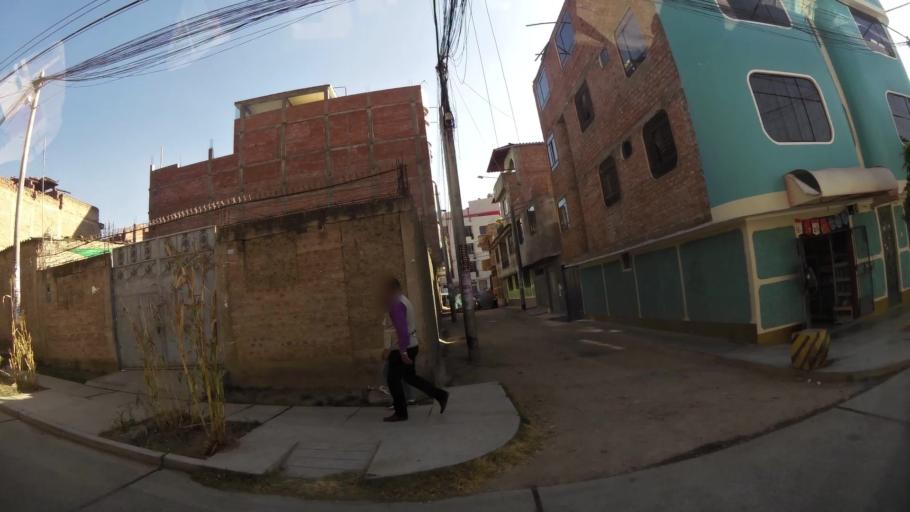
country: PE
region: Ayacucho
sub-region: Provincia de Huamanga
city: Ayacucho
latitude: -13.1509
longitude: -74.2286
